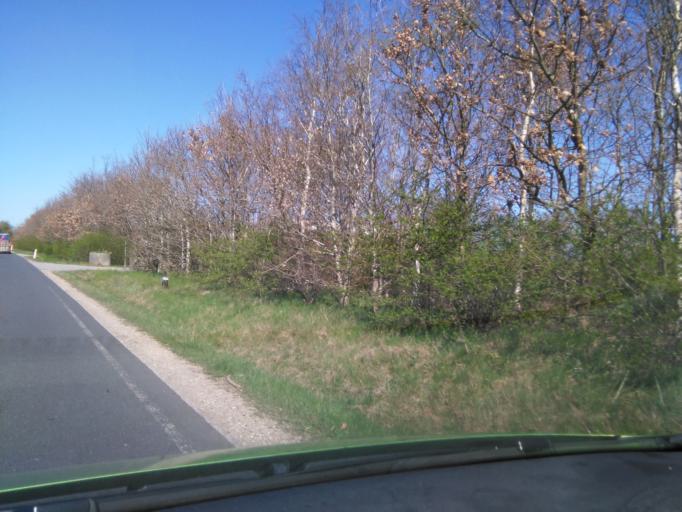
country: DK
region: South Denmark
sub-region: Varde Kommune
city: Olgod
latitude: 55.7105
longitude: 8.7492
